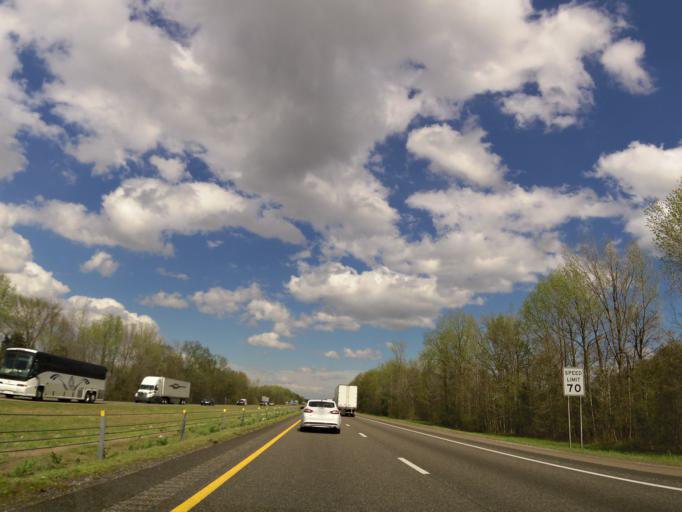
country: US
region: Tennessee
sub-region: Madison County
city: Jackson
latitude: 35.6441
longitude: -88.9109
